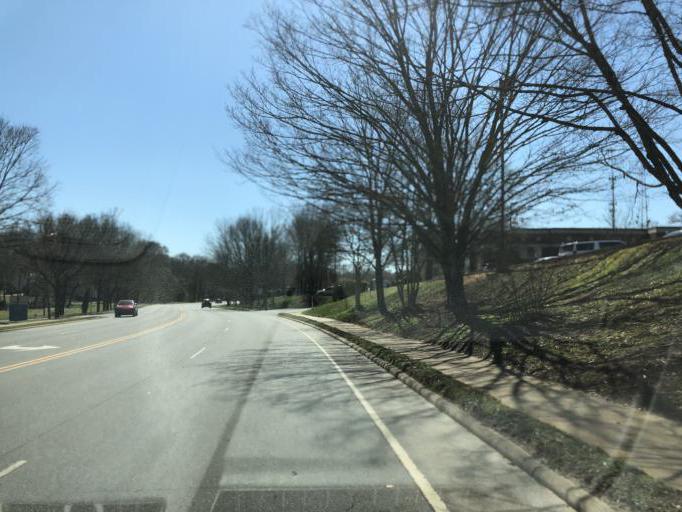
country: US
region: North Carolina
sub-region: Cleveland County
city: Shelby
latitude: 35.3007
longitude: -81.5356
